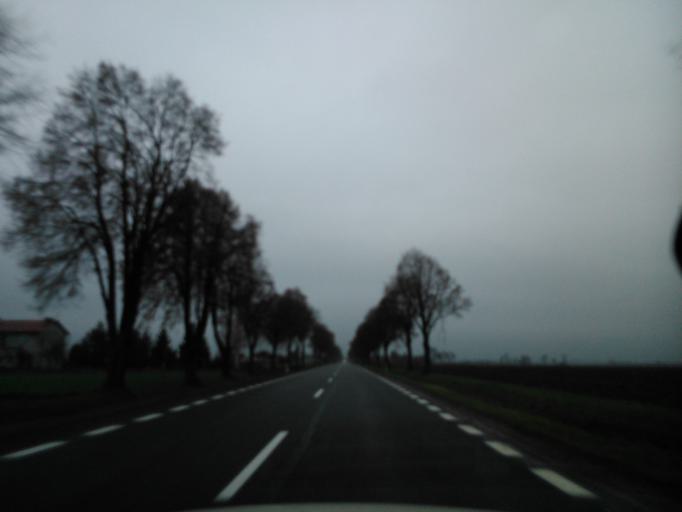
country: PL
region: Swietokrzyskie
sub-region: Powiat opatowski
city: Wojciechowice
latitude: 50.8292
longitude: 21.6087
